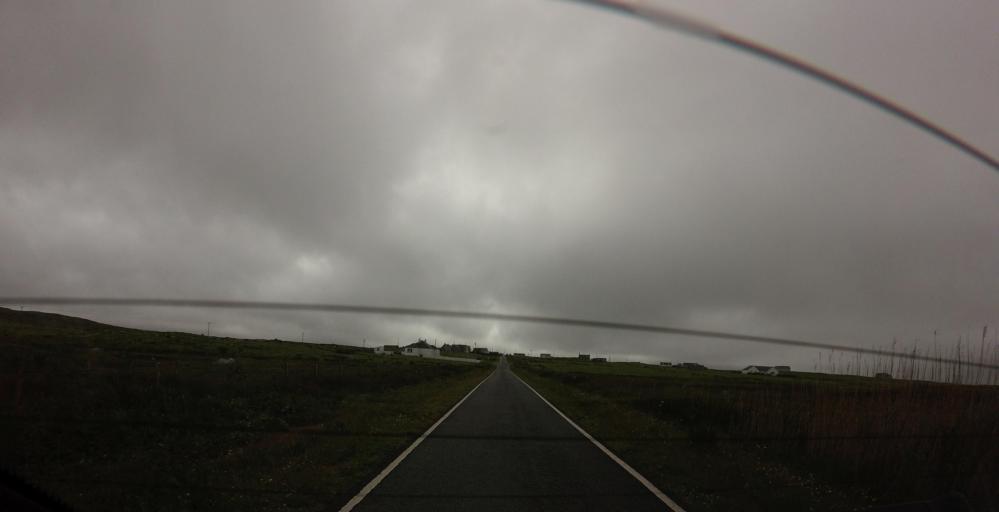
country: GB
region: Scotland
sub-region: Eilean Siar
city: Isle of North Uist
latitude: 57.6495
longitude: -7.3465
